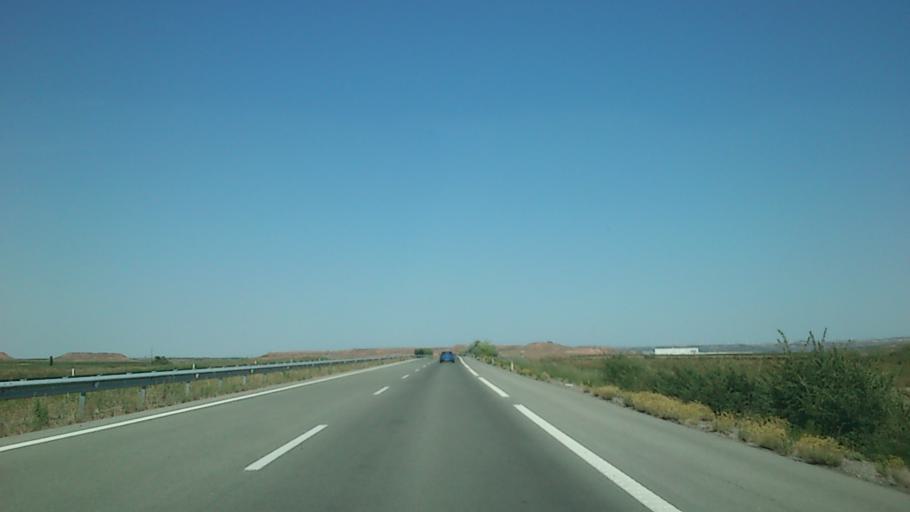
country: ES
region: La Rioja
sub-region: Provincia de La Rioja
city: Rincon de Soto
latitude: 42.1794
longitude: -1.8376
